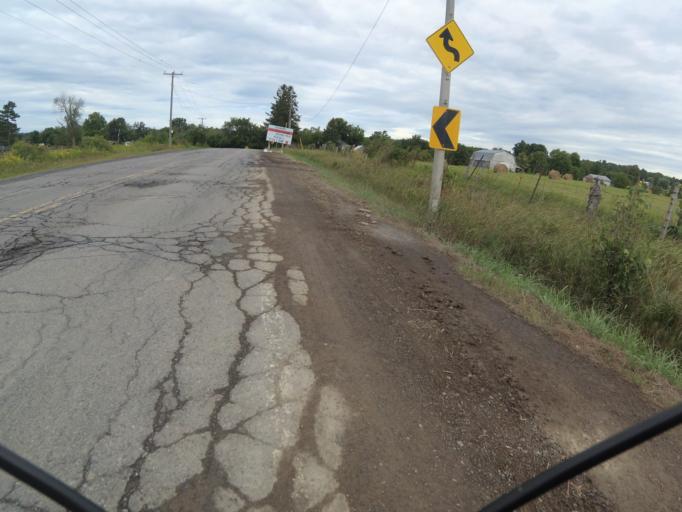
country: CA
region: Ontario
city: Bourget
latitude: 45.3902
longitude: -75.2784
